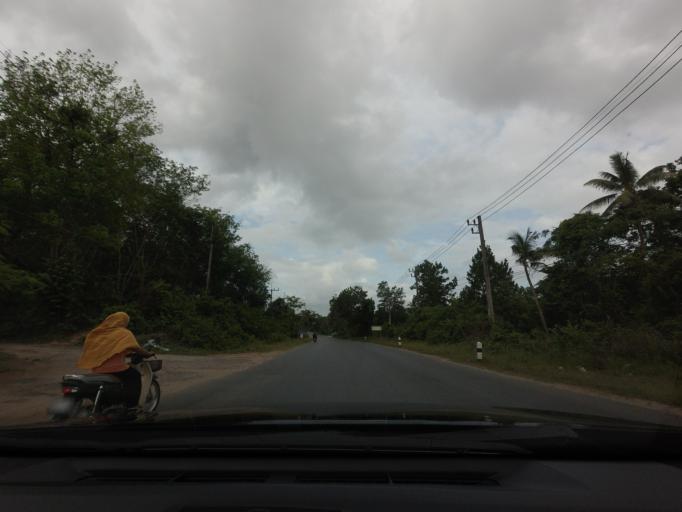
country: TH
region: Yala
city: Raman
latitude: 6.4749
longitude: 101.4034
